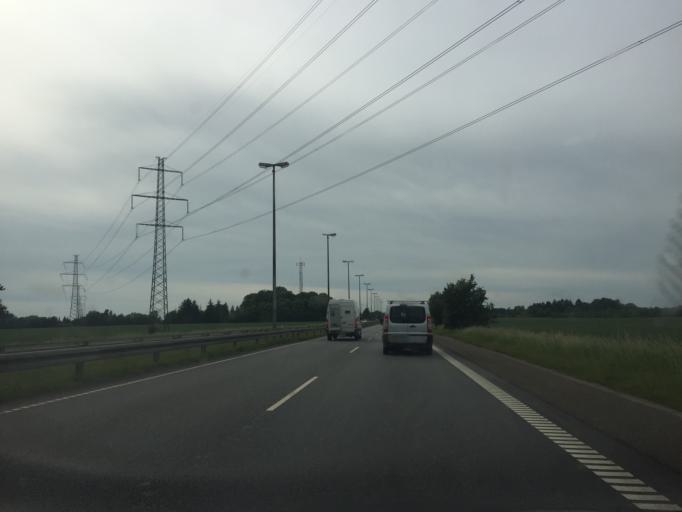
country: DK
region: Capital Region
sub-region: Hoje-Taastrup Kommune
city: Taastrup
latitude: 55.6318
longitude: 12.2940
